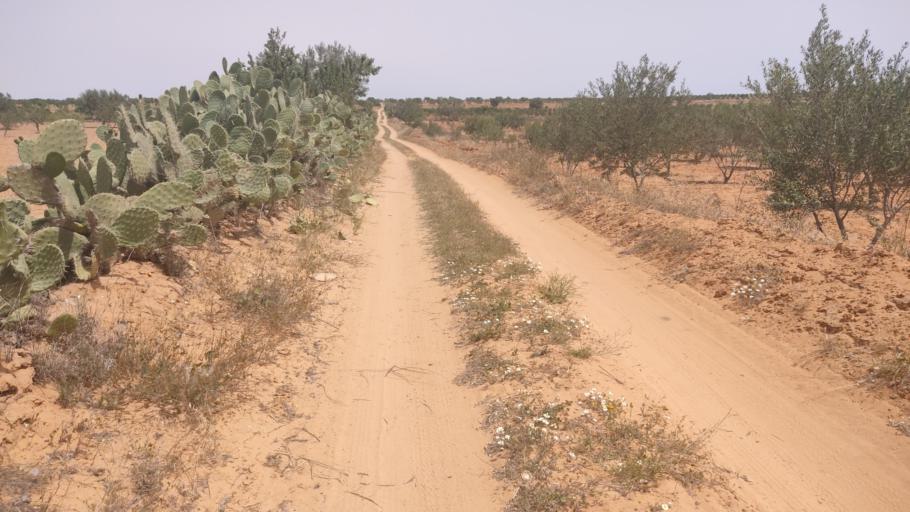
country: TN
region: Safaqis
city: Sfax
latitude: 34.8461
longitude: 10.5945
